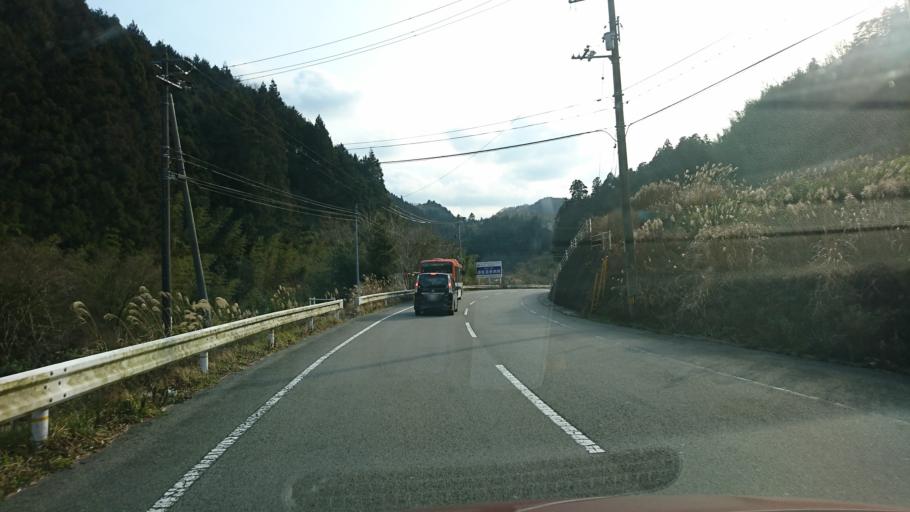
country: JP
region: Ehime
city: Hojo
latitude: 33.9215
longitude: 132.8863
